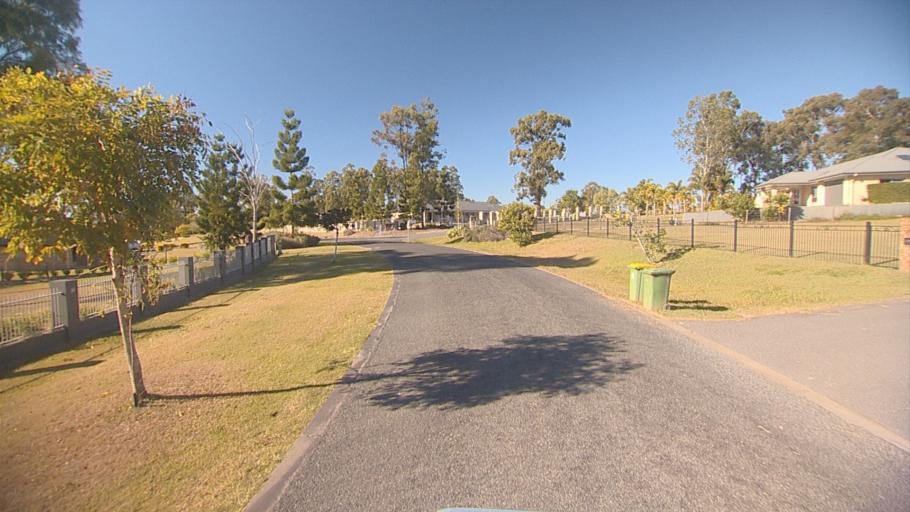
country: AU
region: Queensland
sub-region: Logan
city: North Maclean
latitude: -27.7461
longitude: 152.9579
